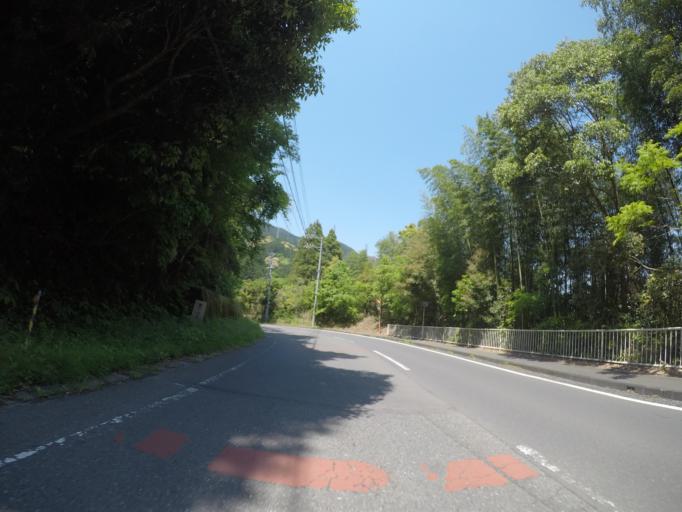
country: JP
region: Shizuoka
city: Shizuoka-shi
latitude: 34.9894
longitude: 138.2915
